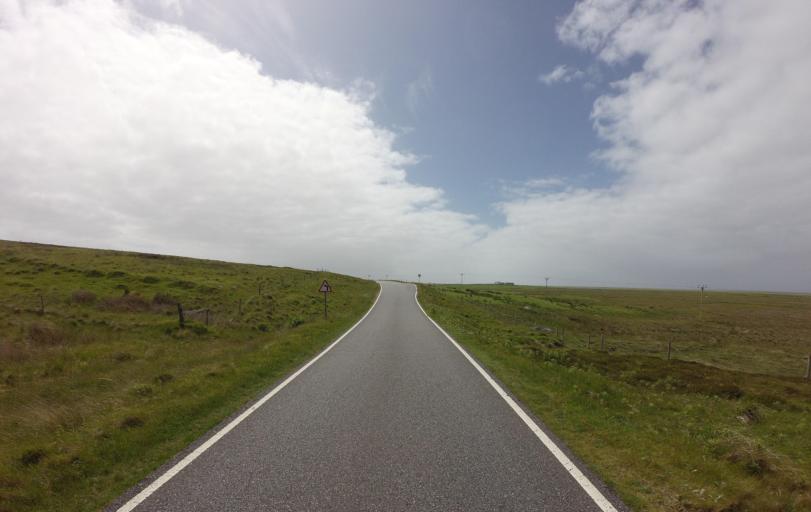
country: GB
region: Scotland
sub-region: Eilean Siar
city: Isle of South Uist
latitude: 57.3439
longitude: -7.3645
